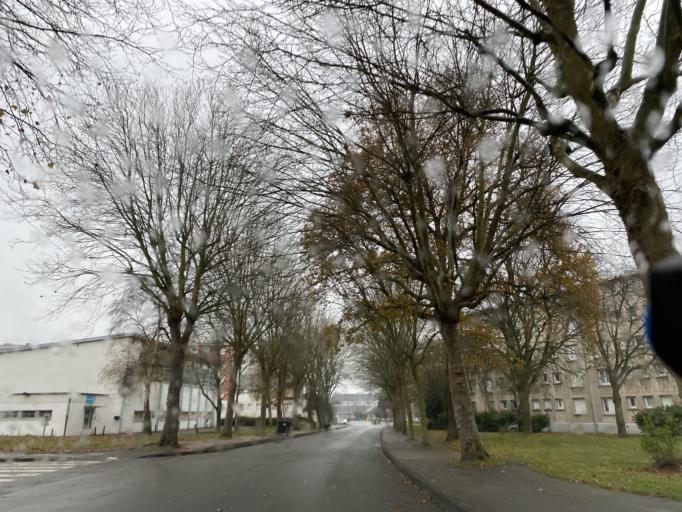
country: FR
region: Haute-Normandie
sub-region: Departement de l'Eure
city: Evreux
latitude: 49.0282
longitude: 1.1713
